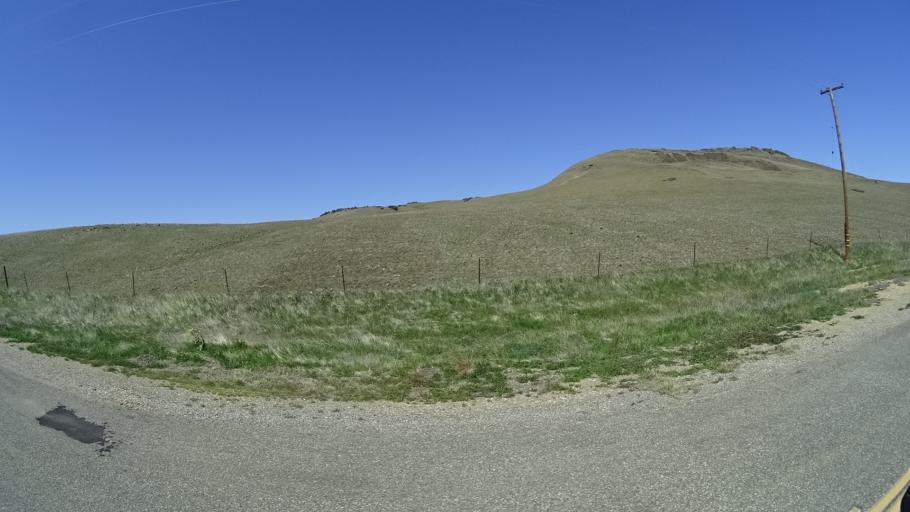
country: US
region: California
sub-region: Glenn County
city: Orland
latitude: 39.7637
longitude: -122.3345
